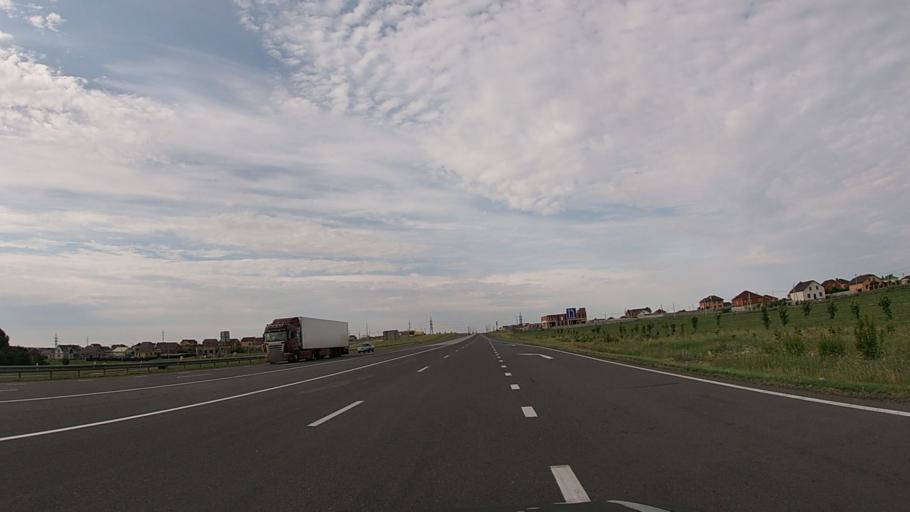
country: RU
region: Belgorod
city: Severnyy
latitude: 50.6700
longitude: 36.4710
